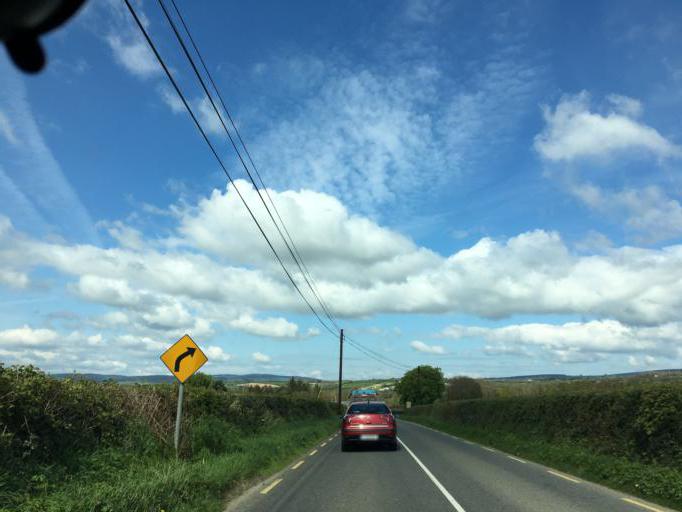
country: IE
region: Leinster
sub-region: Loch Garman
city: New Ross
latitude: 52.4274
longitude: -6.9467
